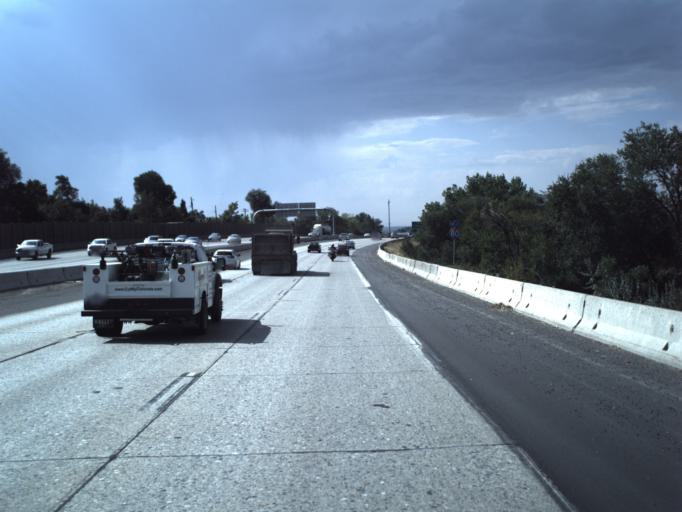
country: US
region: Utah
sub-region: Salt Lake County
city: Willard
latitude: 40.7152
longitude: -111.8299
